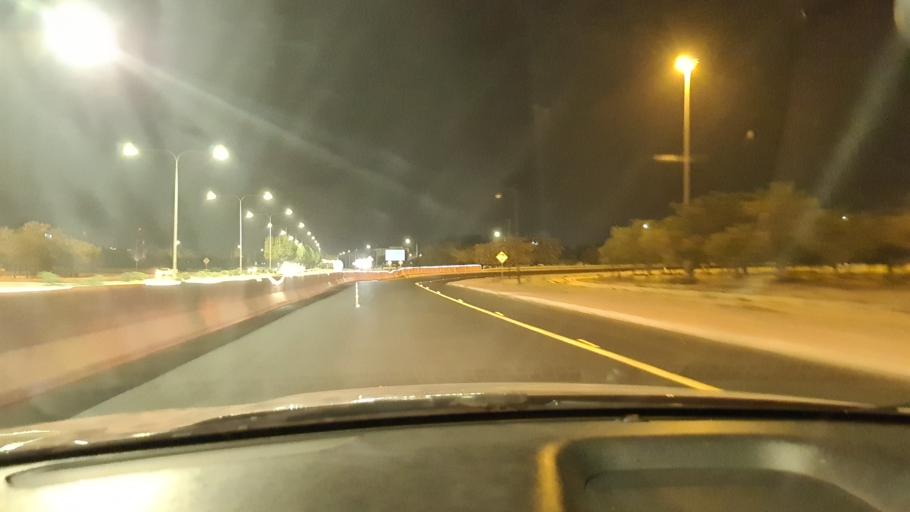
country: SA
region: Eastern Province
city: Al Jubayl
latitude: 27.1371
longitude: 49.5577
